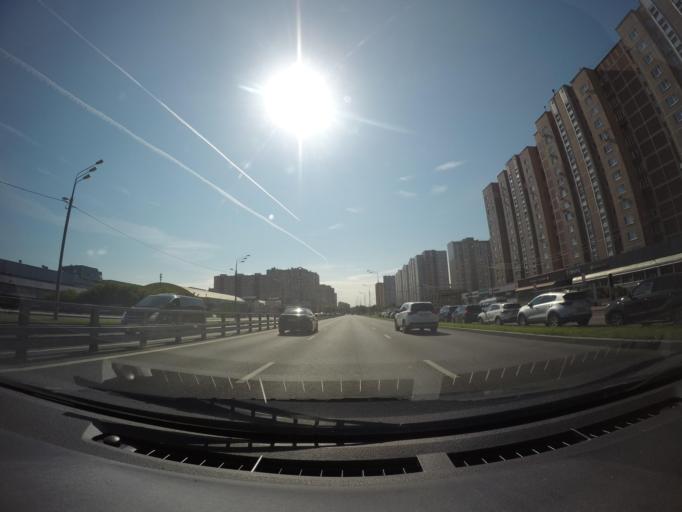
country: RU
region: Moscow
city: Zhulebino
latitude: 55.7012
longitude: 37.8520
